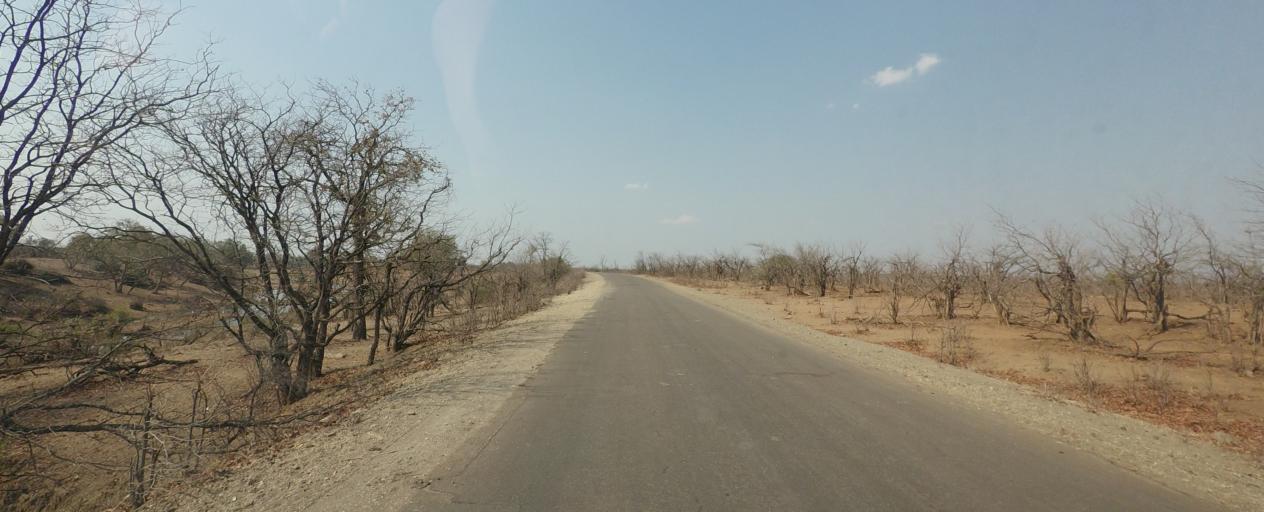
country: ZA
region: Limpopo
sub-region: Mopani District Municipality
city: Giyani
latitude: -23.1384
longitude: 31.3756
